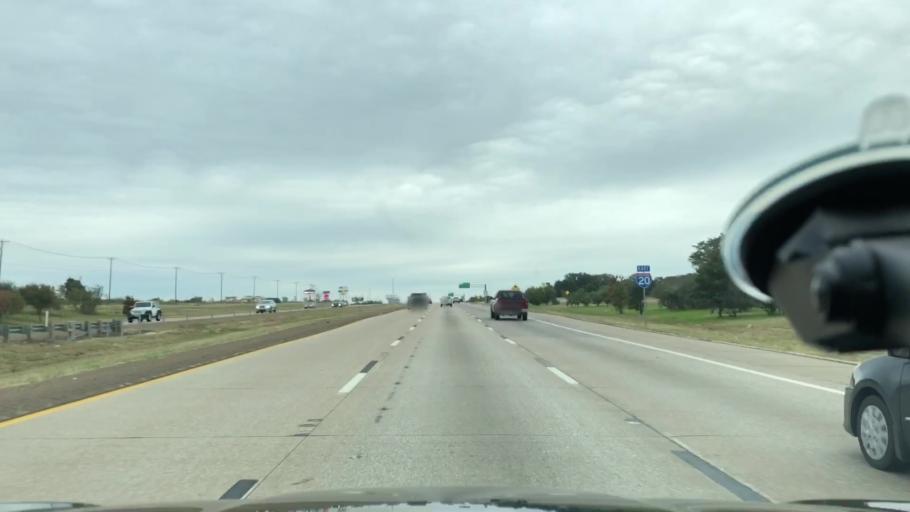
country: US
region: Texas
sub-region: Dallas County
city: Balch Springs
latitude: 32.7033
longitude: -96.5959
